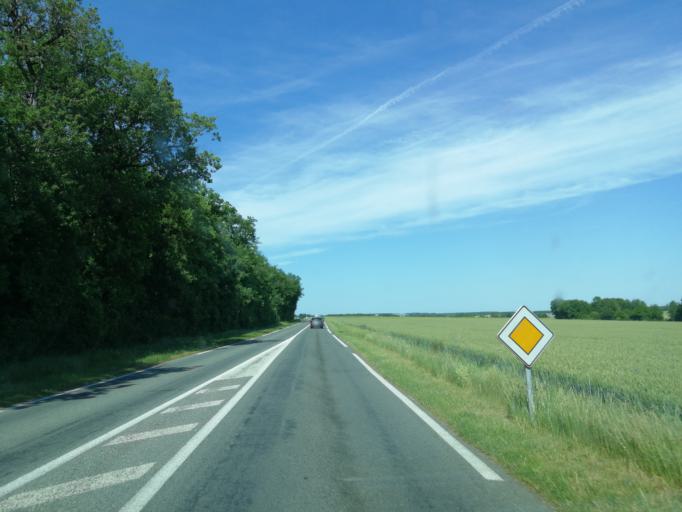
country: FR
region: Poitou-Charentes
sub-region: Departement de la Vienne
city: Loudun
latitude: 47.0430
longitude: 0.1318
